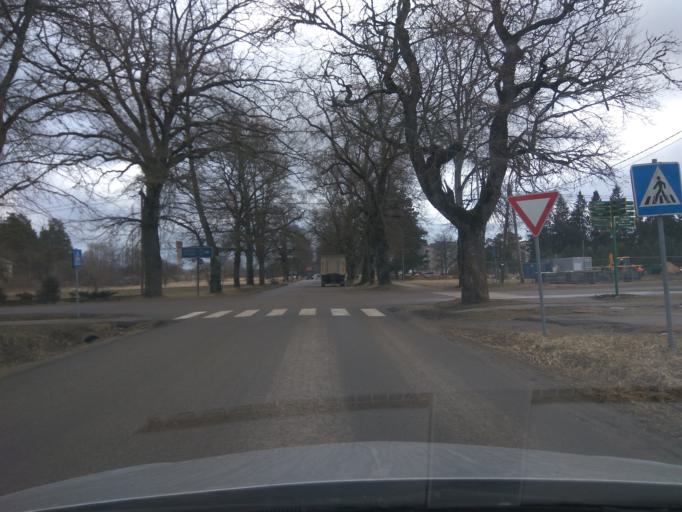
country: LV
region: Kuldigas Rajons
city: Kuldiga
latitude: 57.2769
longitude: 22.0209
